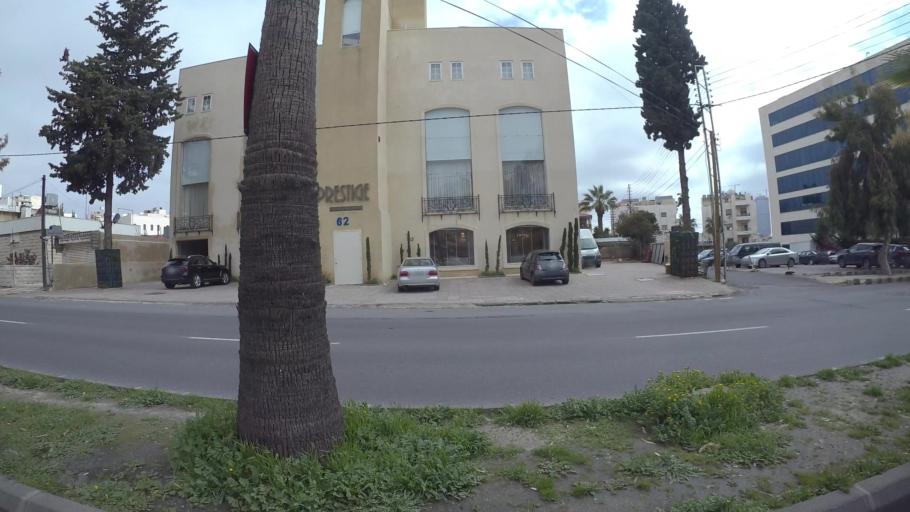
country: JO
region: Amman
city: Wadi as Sir
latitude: 31.9694
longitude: 35.8547
